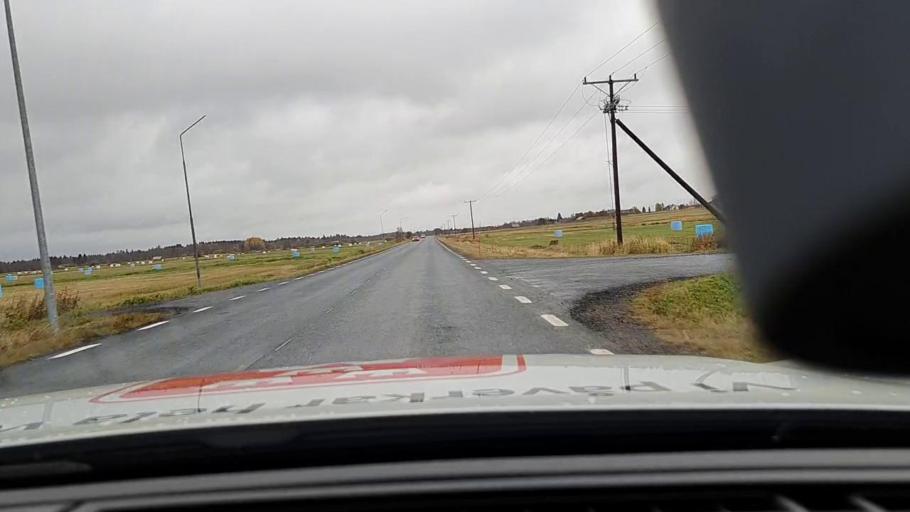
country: FI
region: Lapland
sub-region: Kemi-Tornio
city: Tornio
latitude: 65.9814
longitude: 24.0268
